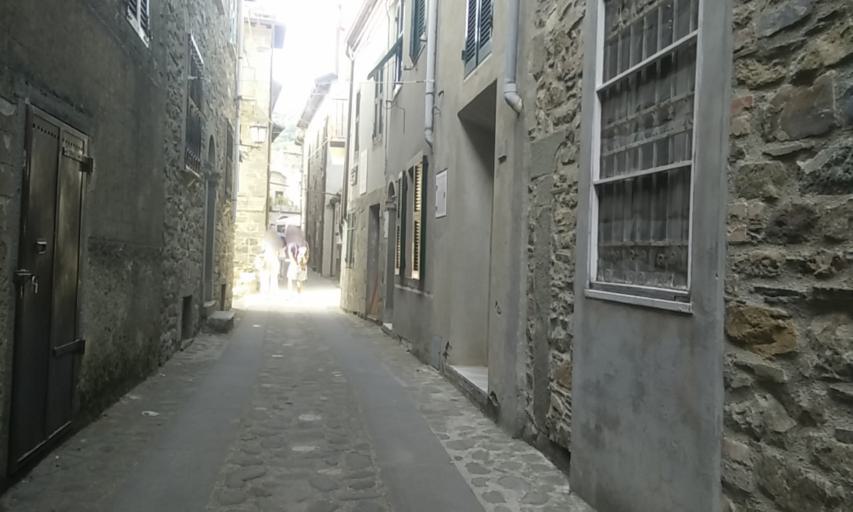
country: IT
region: Tuscany
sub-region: Provincia di Massa-Carrara
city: Mulazzo
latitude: 44.2959
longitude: 9.8430
